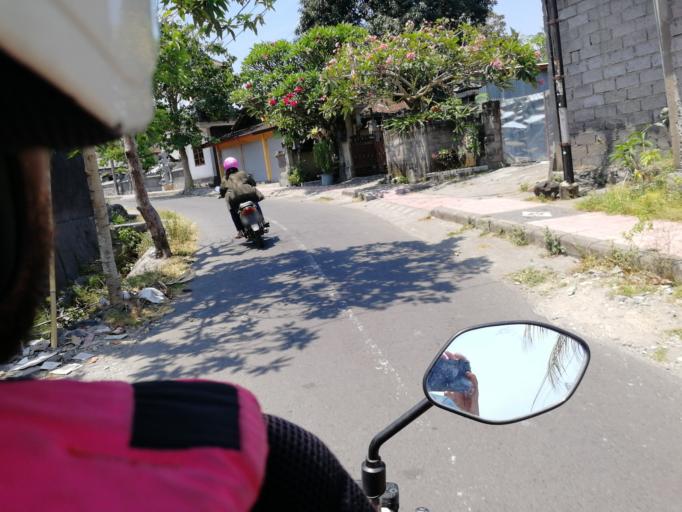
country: ID
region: Bali
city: Subagan
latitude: -8.4607
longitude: 115.5980
